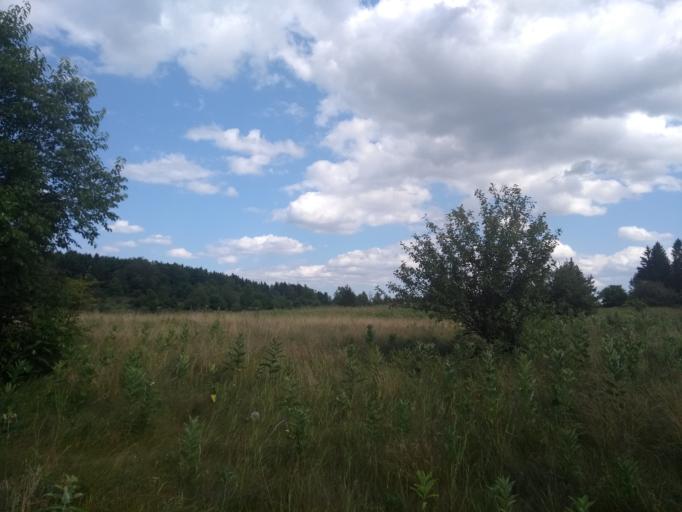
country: CA
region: Ontario
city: Orangeville
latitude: 43.8195
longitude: -80.0047
